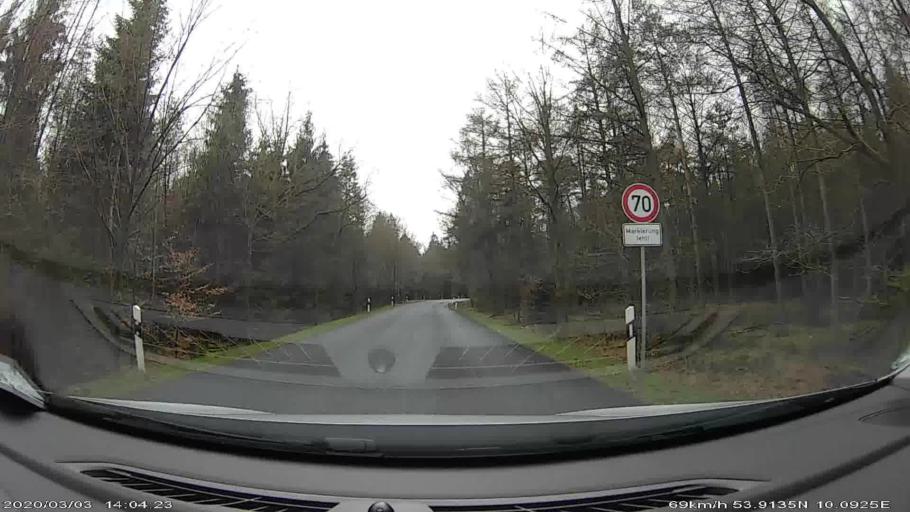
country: DE
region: Schleswig-Holstein
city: Hartenholm
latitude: 53.9128
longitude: 10.0925
